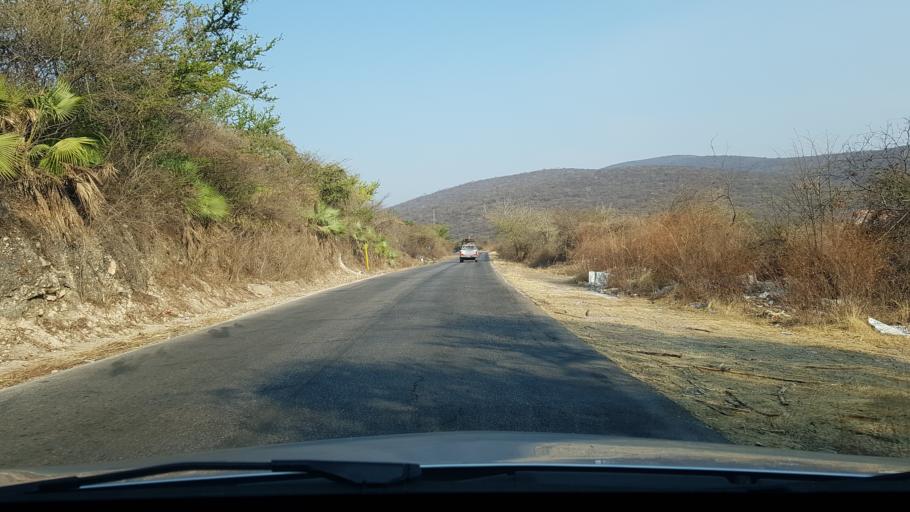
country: MX
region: Morelos
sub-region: Tlaltizapan de Zapata
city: Colonia Palo Prieto (Chipitongo)
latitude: 18.6739
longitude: -99.0601
